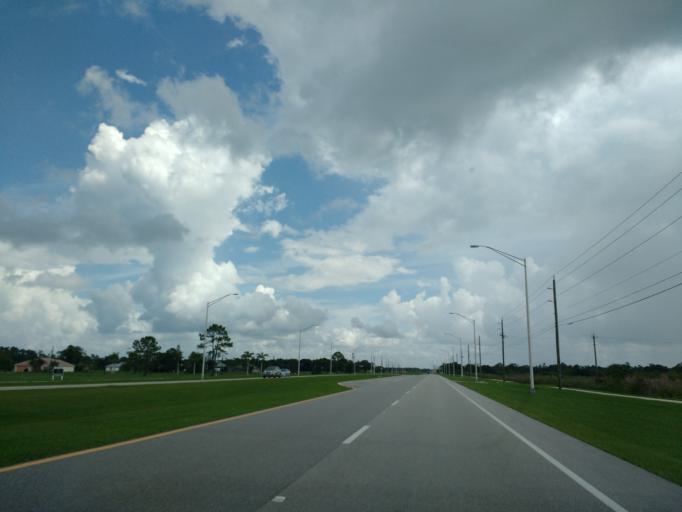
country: US
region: Florida
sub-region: Lee County
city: Burnt Store Marina
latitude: 26.7786
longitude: -82.0379
